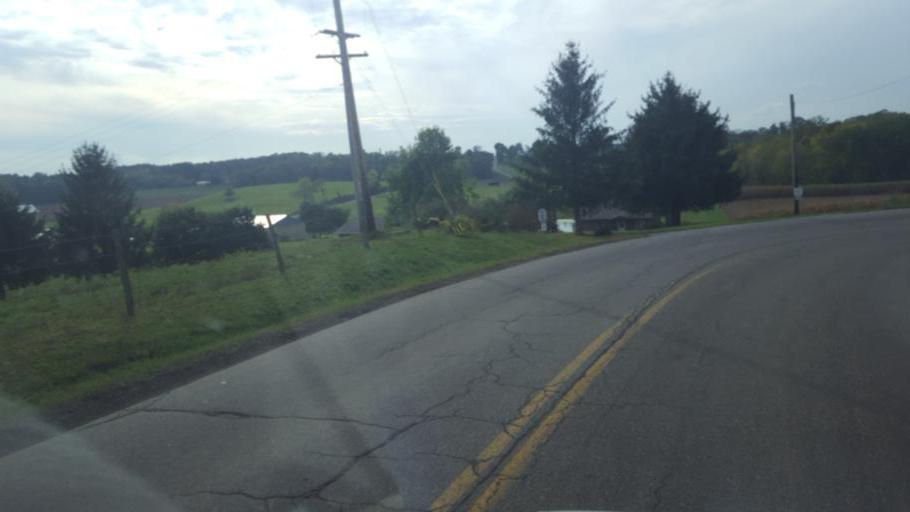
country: US
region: Ohio
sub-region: Holmes County
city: Millersburg
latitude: 40.5874
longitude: -81.8295
